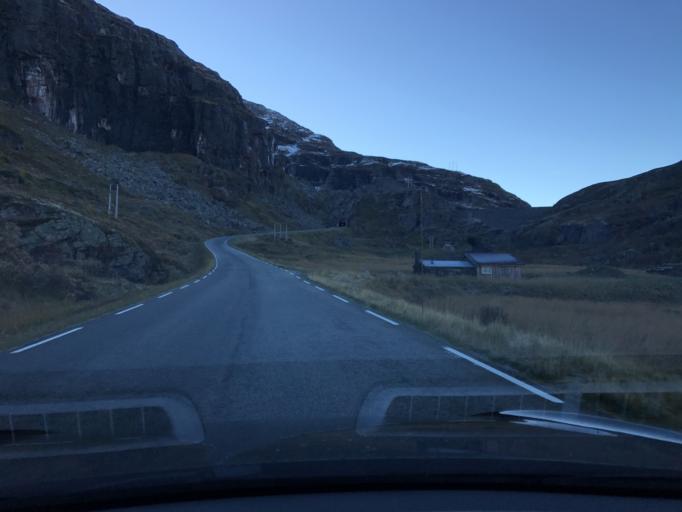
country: NO
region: Sogn og Fjordane
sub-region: Laerdal
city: Laerdalsoyri
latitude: 60.8034
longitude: 7.5648
